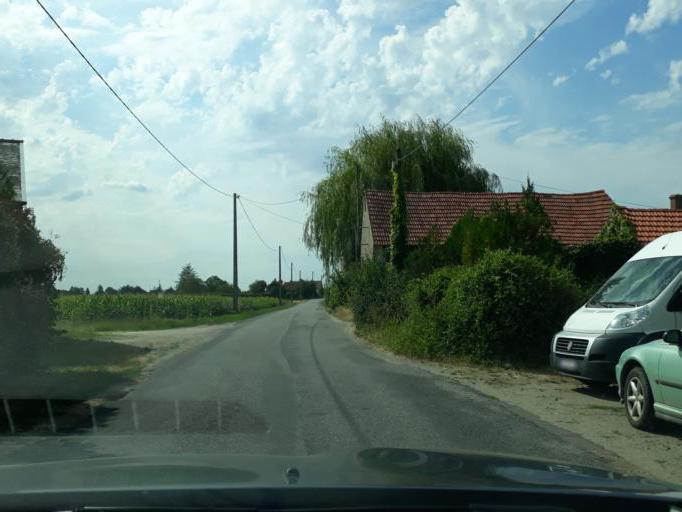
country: FR
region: Centre
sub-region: Departement du Loiret
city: Chateauneuf-sur-Loire
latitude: 47.8434
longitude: 2.1748
